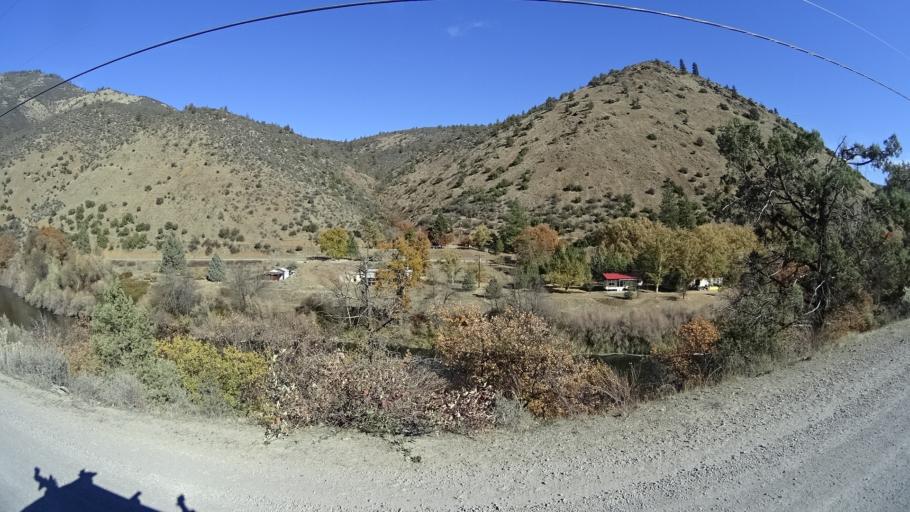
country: US
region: California
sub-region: Siskiyou County
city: Yreka
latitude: 41.8331
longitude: -122.6349
